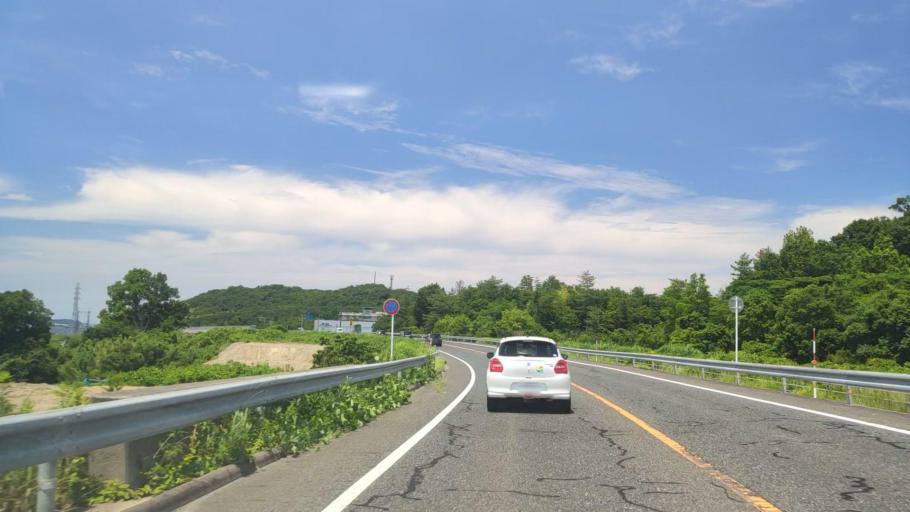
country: JP
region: Tottori
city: Tottori
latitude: 35.4457
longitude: 134.2560
